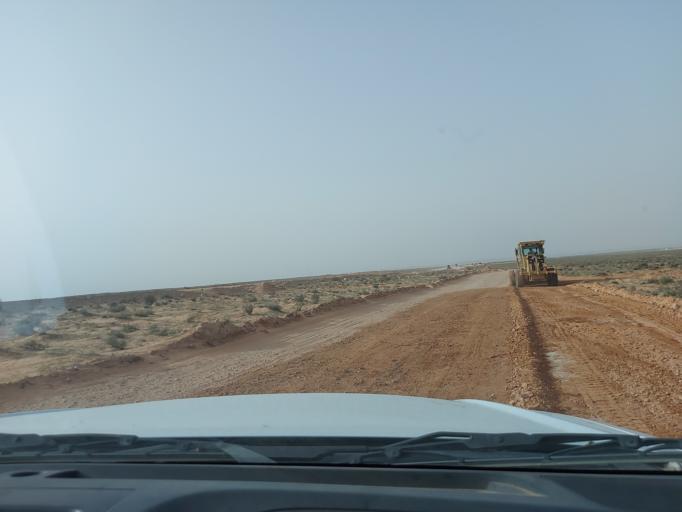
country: TN
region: Madanin
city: Medenine
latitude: 33.2613
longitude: 10.5761
